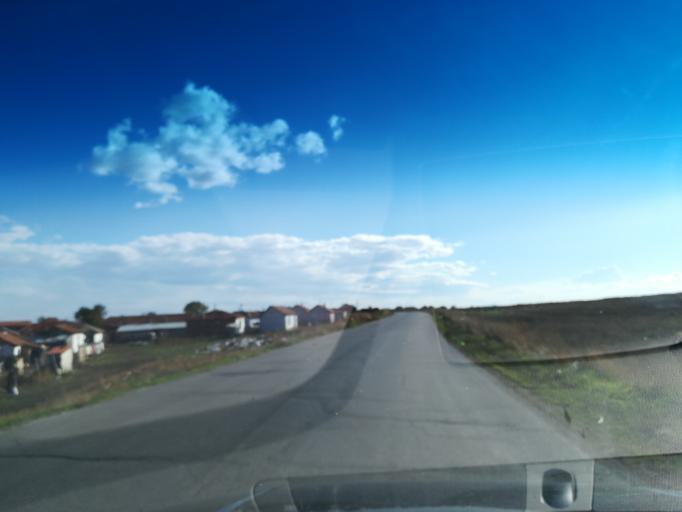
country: BG
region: Stara Zagora
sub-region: Obshtina Chirpan
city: Chirpan
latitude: 42.2042
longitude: 25.3088
